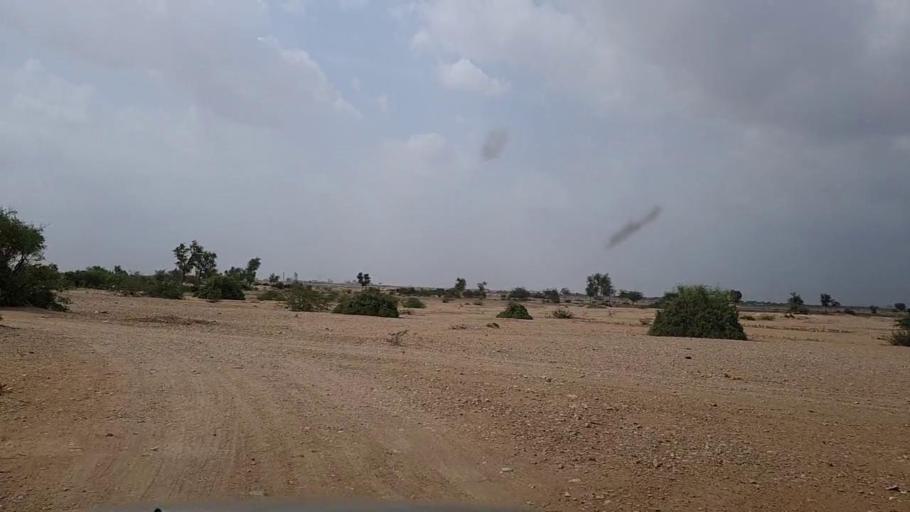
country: PK
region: Sindh
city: Kotri
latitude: 25.2897
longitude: 68.2199
